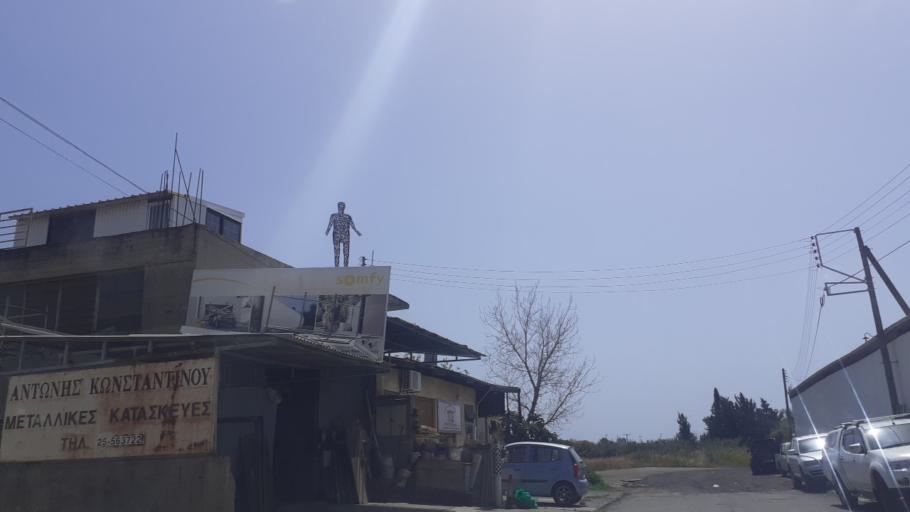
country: CY
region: Limassol
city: Limassol
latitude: 34.6691
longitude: 33.0165
